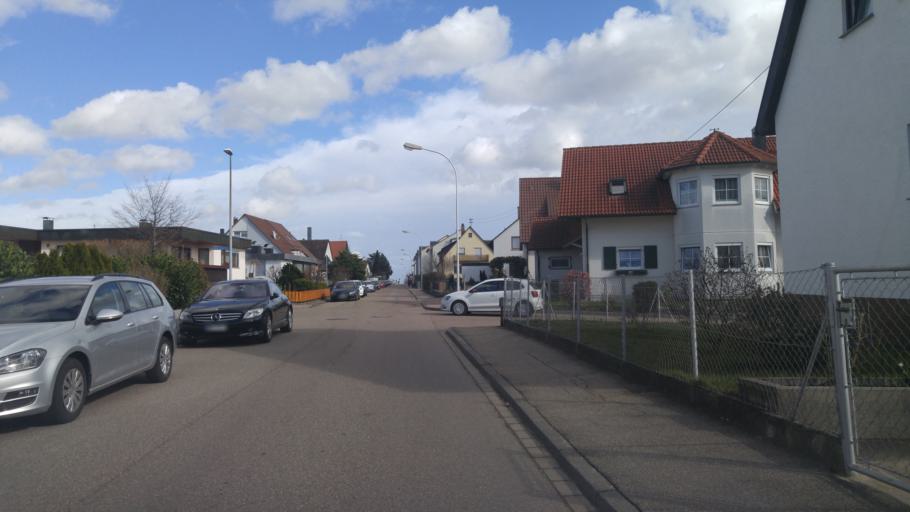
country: DE
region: Baden-Wuerttemberg
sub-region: Regierungsbezirk Stuttgart
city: Rutesheim
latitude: 48.8092
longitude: 8.9508
